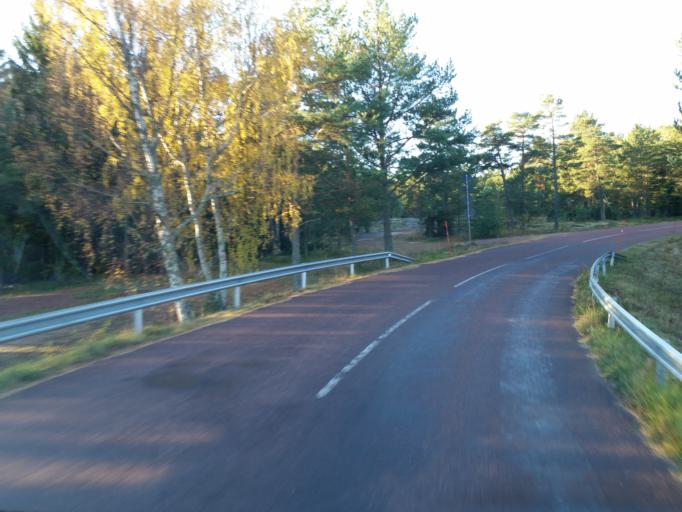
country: AX
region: Alands skaergard
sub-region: Vardoe
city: Vardoe
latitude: 60.2712
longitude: 20.3898
